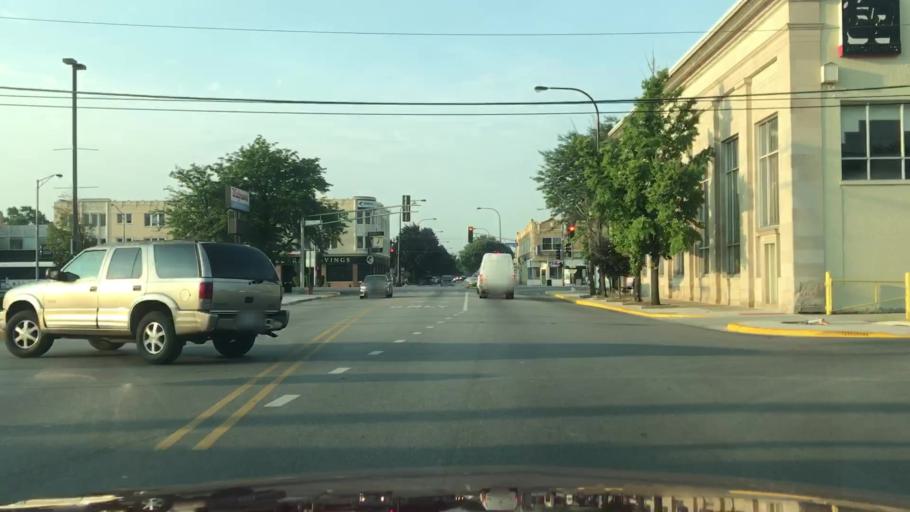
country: US
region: Illinois
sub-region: Cook County
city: Berwyn
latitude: 41.8517
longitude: -87.7738
